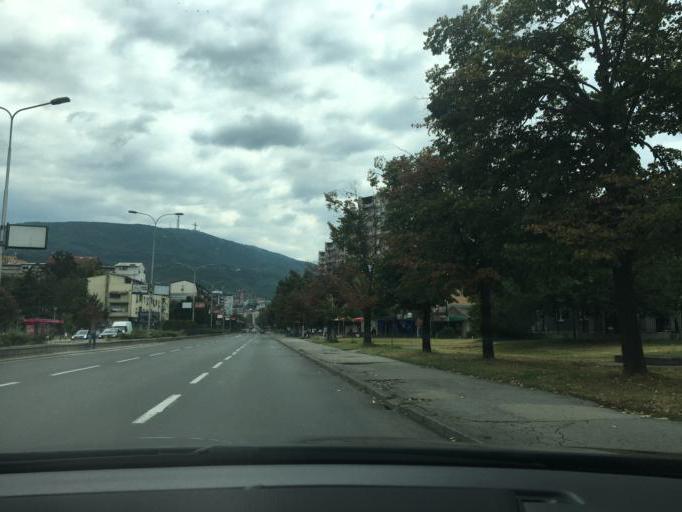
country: MK
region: Karpos
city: Skopje
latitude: 41.9928
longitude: 21.4393
